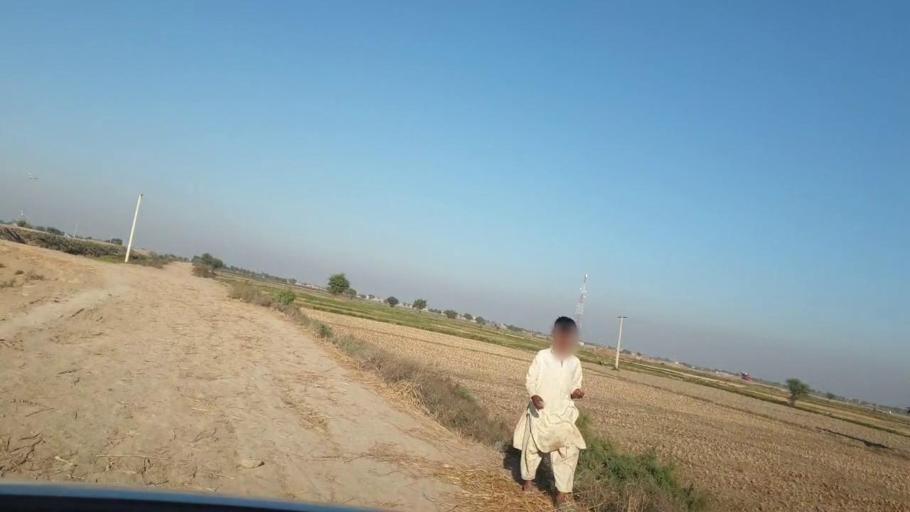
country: PK
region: Sindh
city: Khairpur Nathan Shah
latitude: 27.0372
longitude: 67.7121
